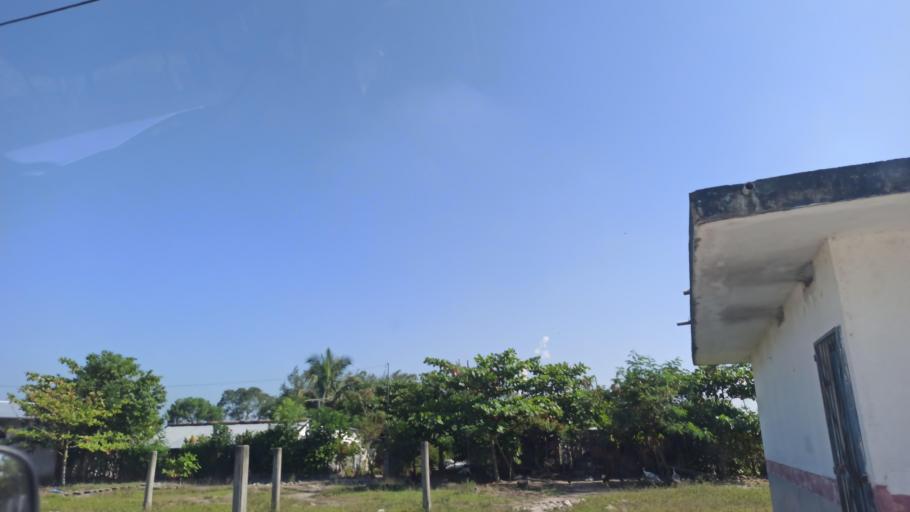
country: MX
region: Veracruz
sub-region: Martinez de la Torre
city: La Union Paso Largo
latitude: 20.1419
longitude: -96.9999
